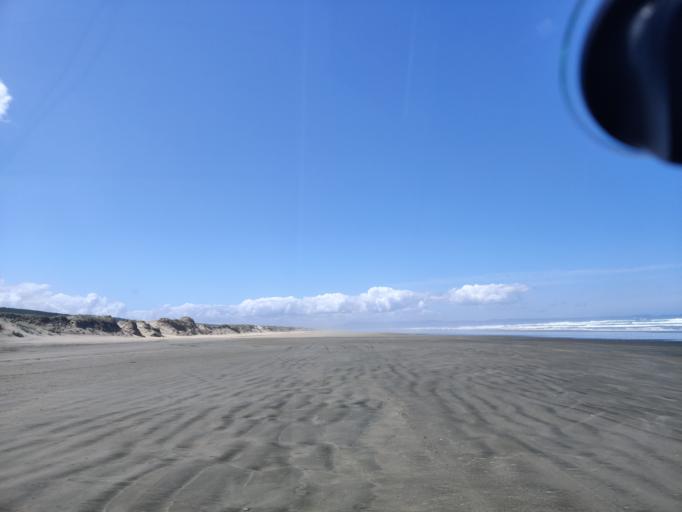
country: NZ
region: Northland
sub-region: Far North District
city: Kaitaia
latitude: -34.9530
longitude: 173.1234
